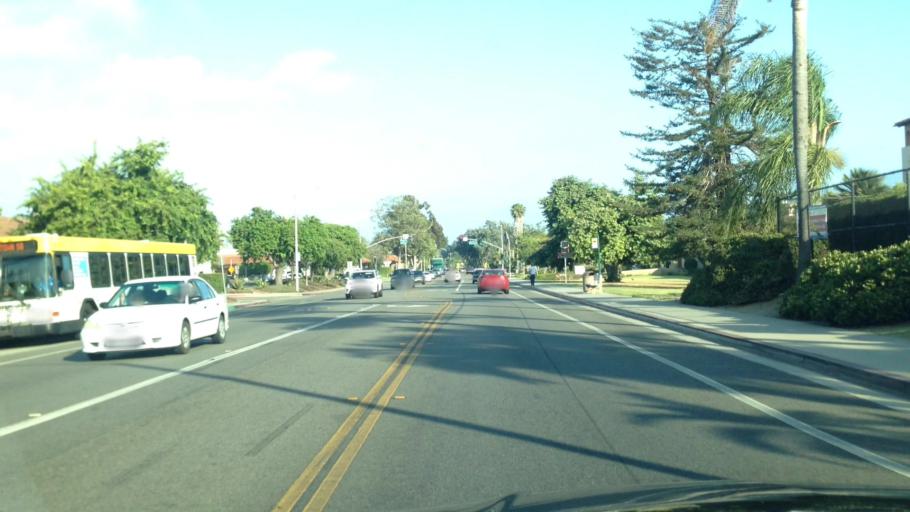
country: US
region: California
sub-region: Santa Barbara County
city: Carpinteria
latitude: 34.3965
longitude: -119.5156
